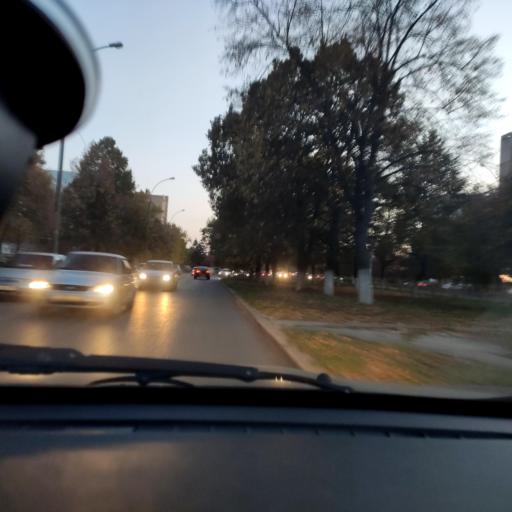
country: RU
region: Samara
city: Tol'yatti
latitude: 53.5284
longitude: 49.3127
